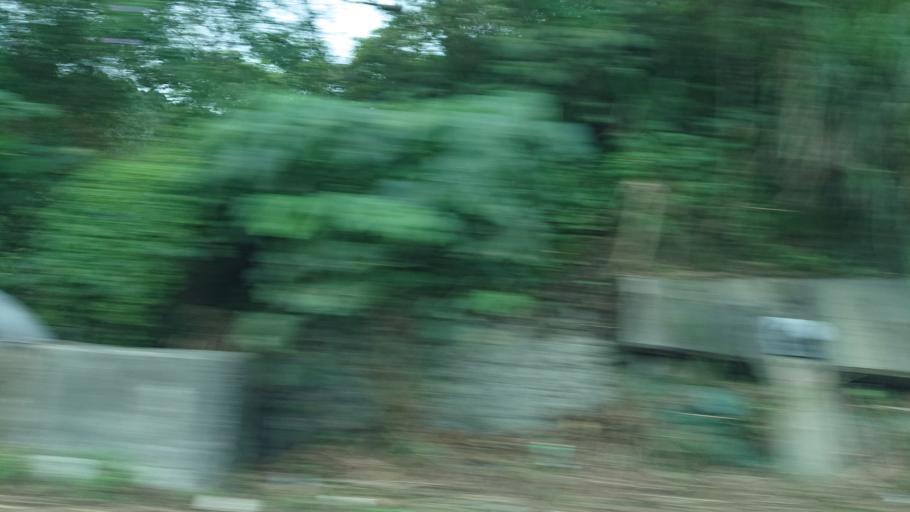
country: TW
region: Taiwan
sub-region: Keelung
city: Keelung
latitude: 25.0983
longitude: 121.7026
